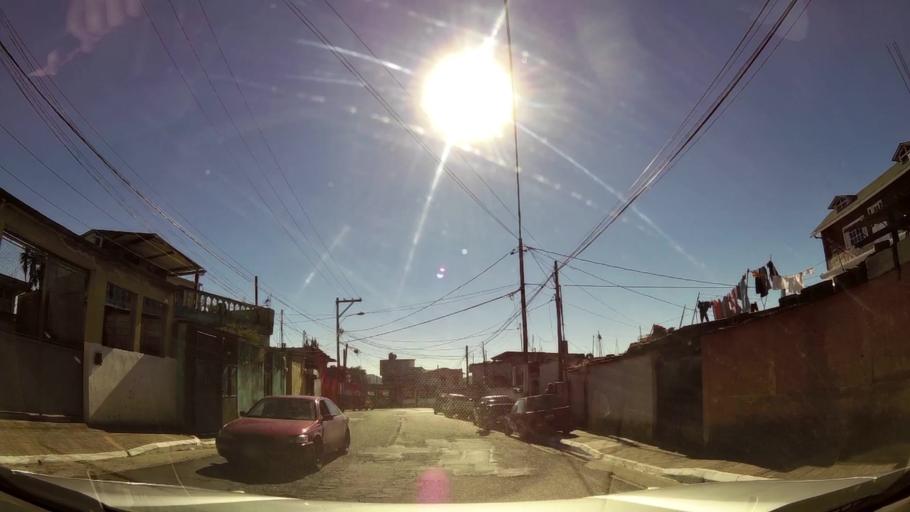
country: GT
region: Guatemala
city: Fraijanes
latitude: 14.4710
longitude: -90.4466
